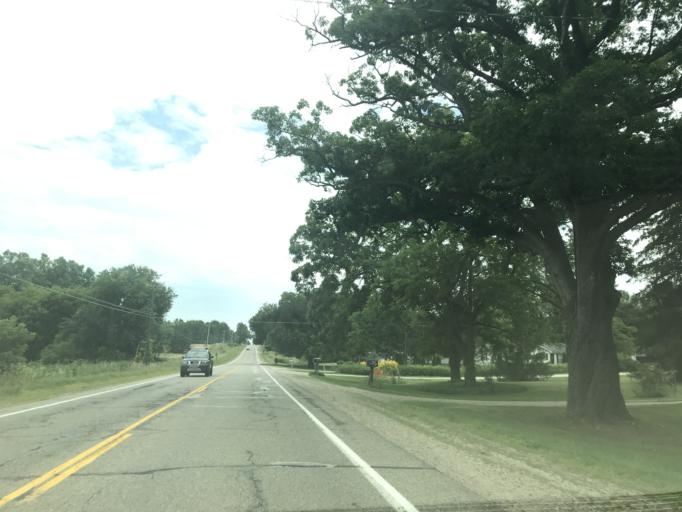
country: US
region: Michigan
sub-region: Clinton County
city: Wacousta
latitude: 42.7920
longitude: -84.7079
